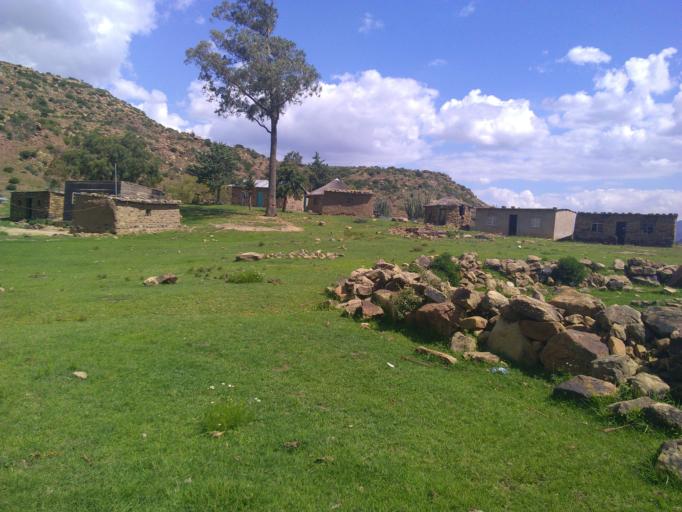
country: LS
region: Quthing
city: Quthing
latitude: -30.3390
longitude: 27.5339
